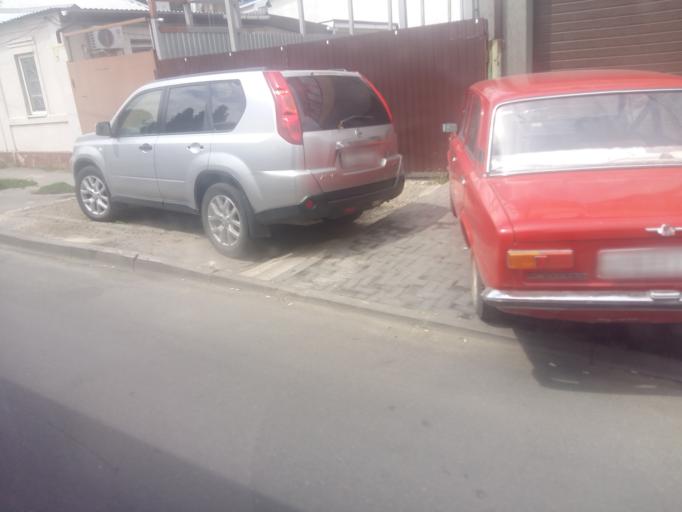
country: RU
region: Rostov
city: Imeni Chkalova
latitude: 47.2734
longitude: 39.7474
